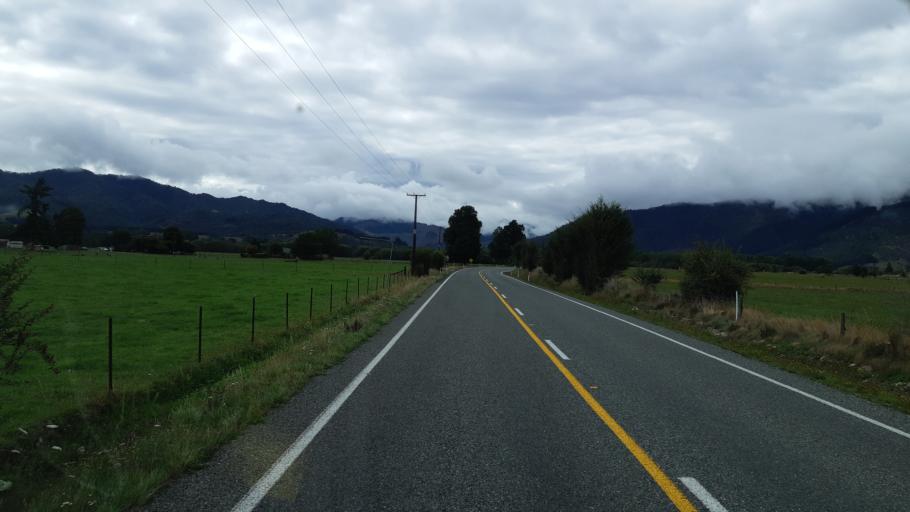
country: NZ
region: West Coast
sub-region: Buller District
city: Westport
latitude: -41.7947
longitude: 172.3048
